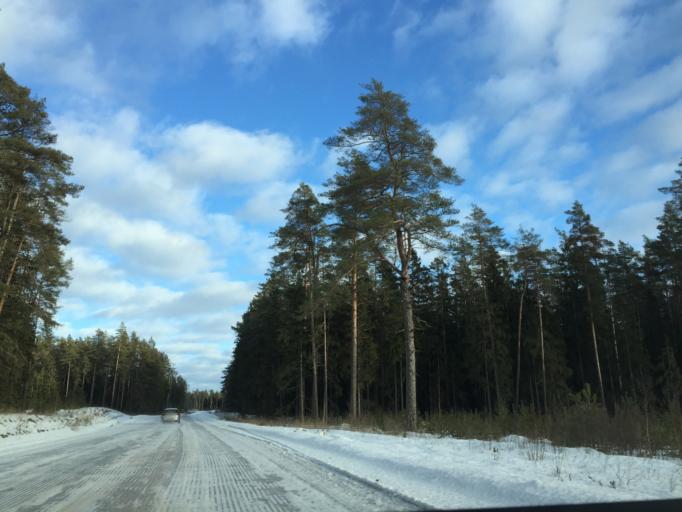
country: LV
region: Ogre
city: Jumprava
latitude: 56.5874
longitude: 24.9686
